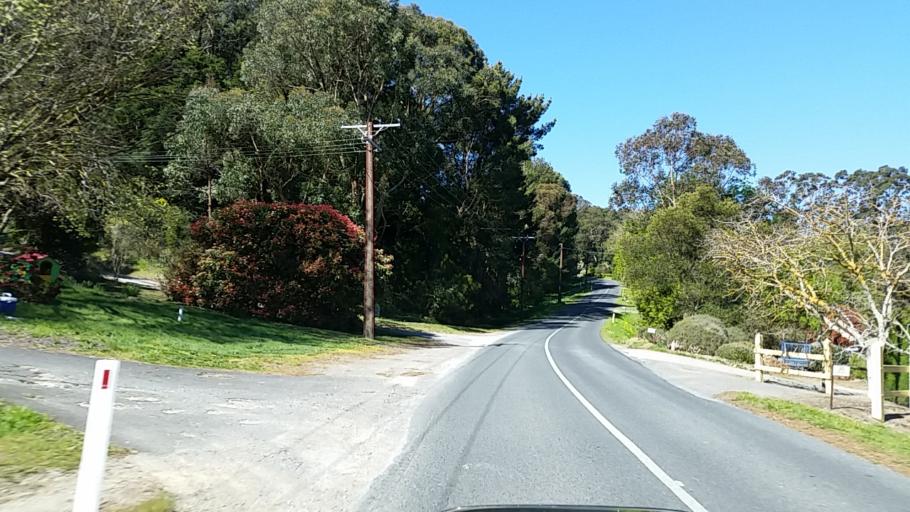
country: AU
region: South Australia
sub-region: Adelaide Hills
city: Bridgewater
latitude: -34.9572
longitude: 138.7468
